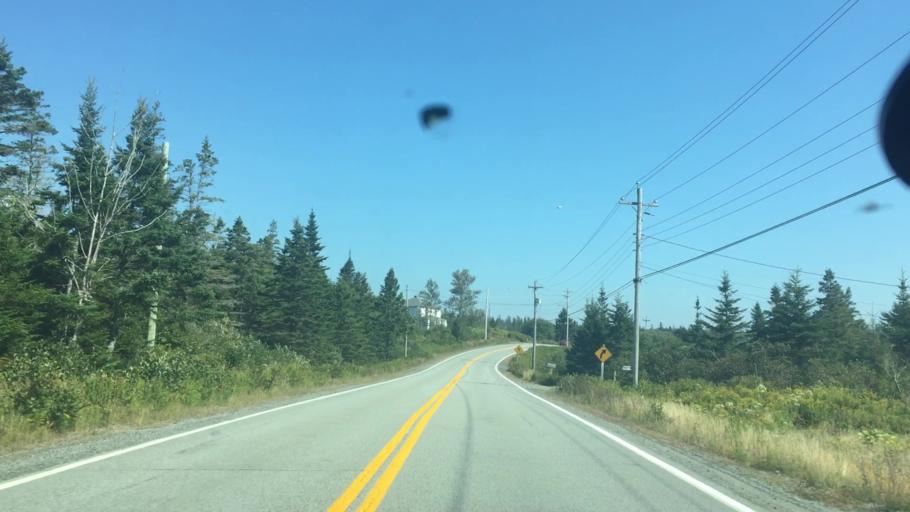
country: CA
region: Nova Scotia
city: New Glasgow
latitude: 44.9295
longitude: -62.2967
